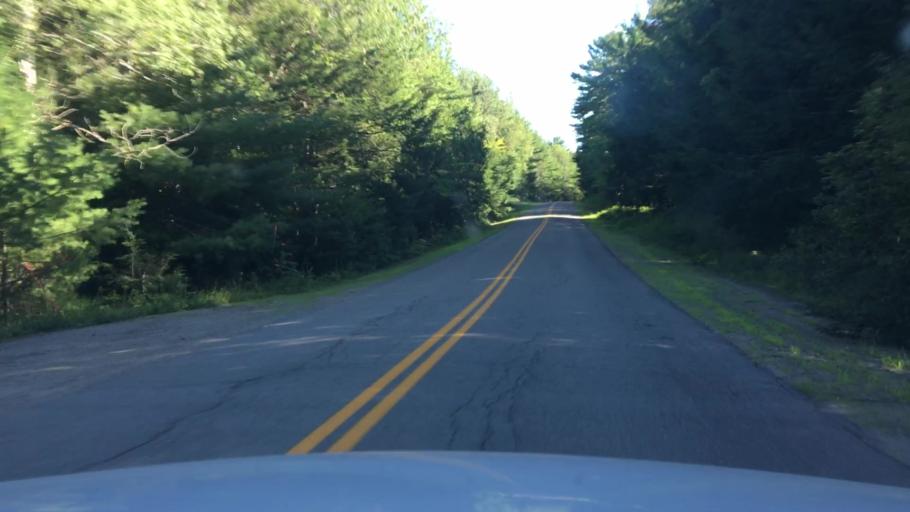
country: US
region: Maine
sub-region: Penobscot County
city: Enfield
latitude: 45.2250
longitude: -68.5801
